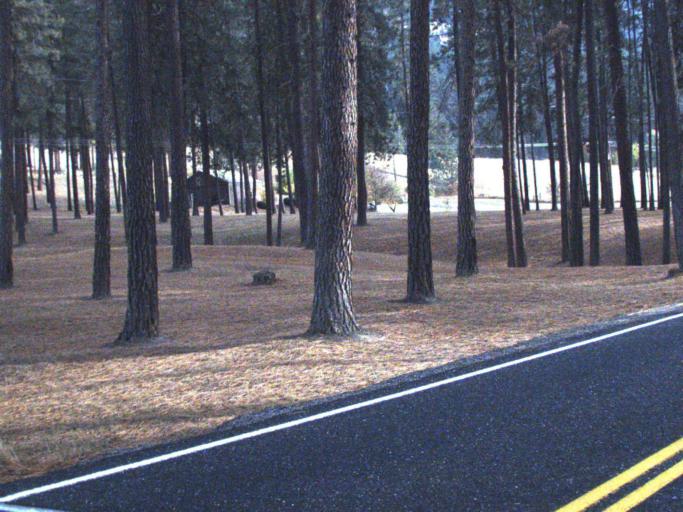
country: US
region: Washington
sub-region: Stevens County
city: Kettle Falls
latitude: 48.2626
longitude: -118.1315
